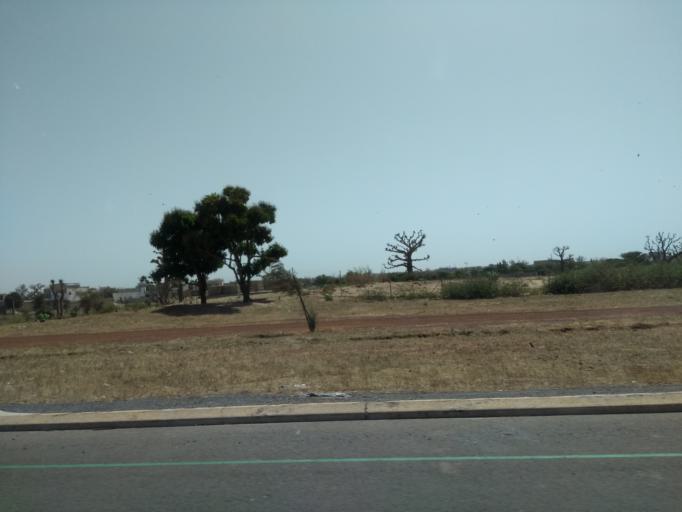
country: SN
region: Thies
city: Thies
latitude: 14.7370
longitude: -17.1803
